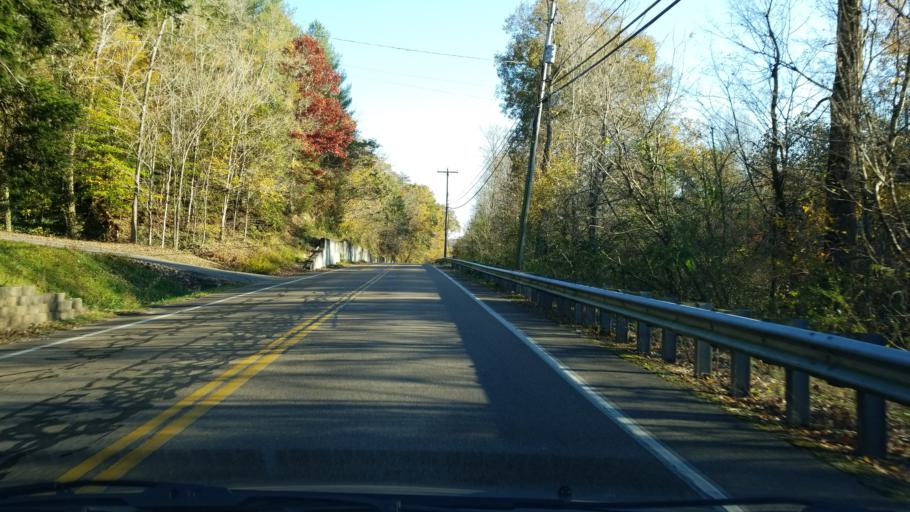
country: US
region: Tennessee
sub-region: Hamilton County
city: Falling Water
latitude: 35.1982
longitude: -85.2472
